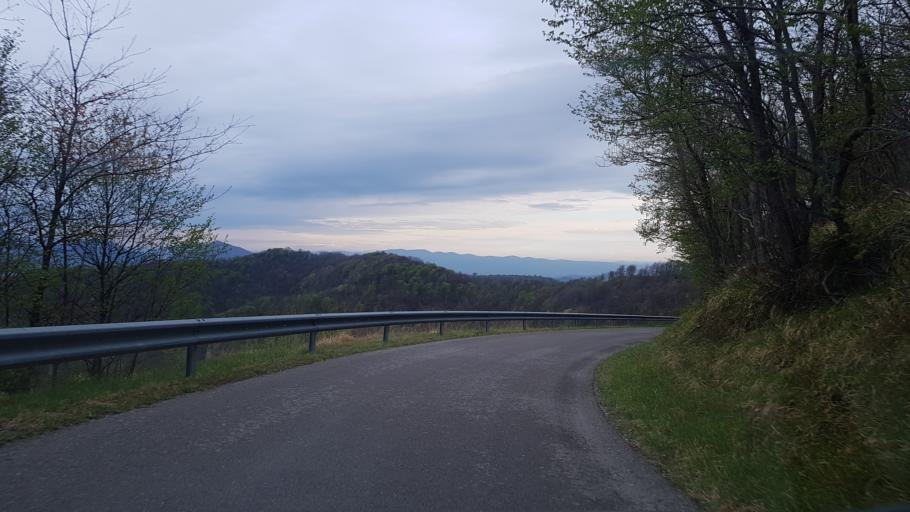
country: SI
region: Kanal
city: Deskle
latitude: 46.0413
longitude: 13.5673
